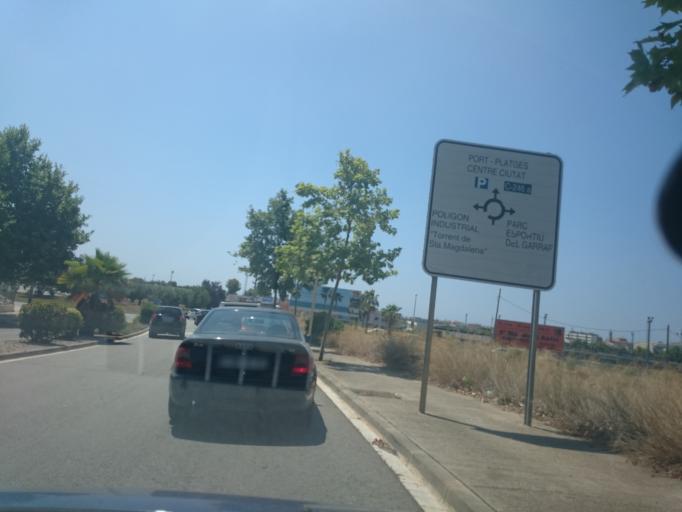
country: ES
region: Catalonia
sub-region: Provincia de Barcelona
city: Vilanova i la Geltru
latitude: 41.2350
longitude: 1.7335
